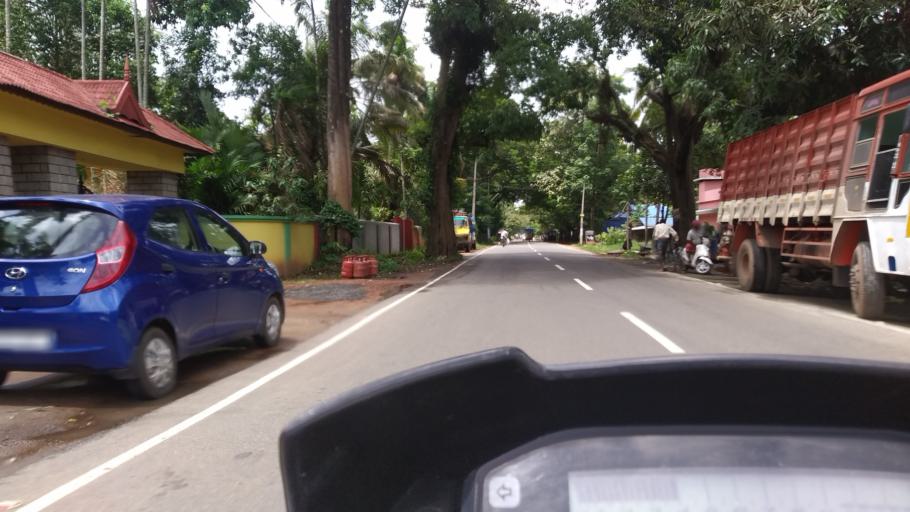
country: IN
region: Kerala
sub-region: Ernakulam
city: Elur
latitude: 10.1309
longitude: 76.2838
